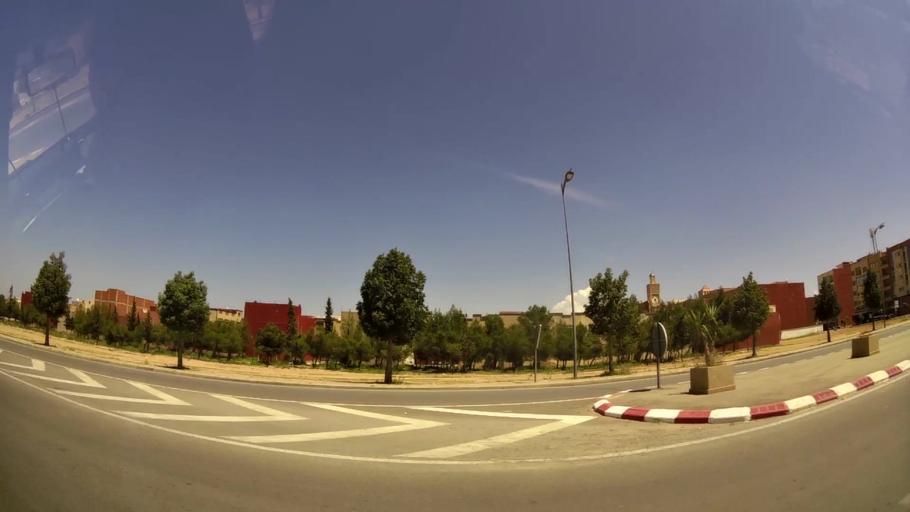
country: MA
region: Oriental
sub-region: Oujda-Angad
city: Oujda
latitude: 34.6837
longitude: -1.9458
